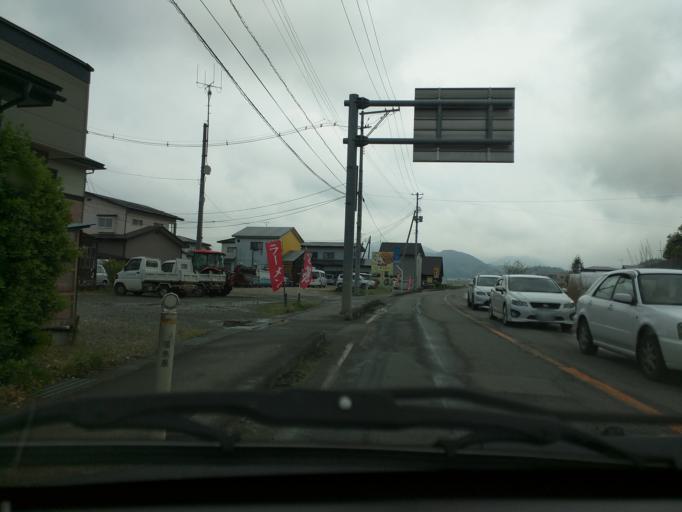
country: JP
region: Fukushima
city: Kitakata
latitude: 37.4483
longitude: 139.8813
